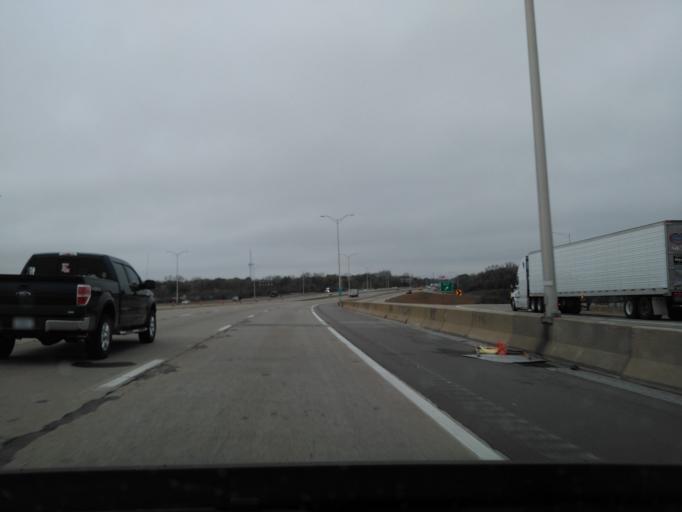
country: US
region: Illinois
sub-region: Saint Clair County
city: Washington Park
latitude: 38.6177
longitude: -90.0695
